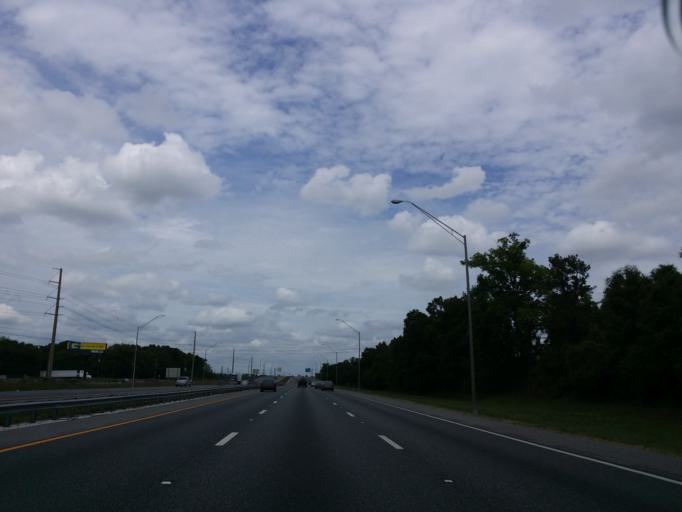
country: US
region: Florida
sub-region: Marion County
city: Ocala
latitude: 29.1615
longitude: -82.1851
